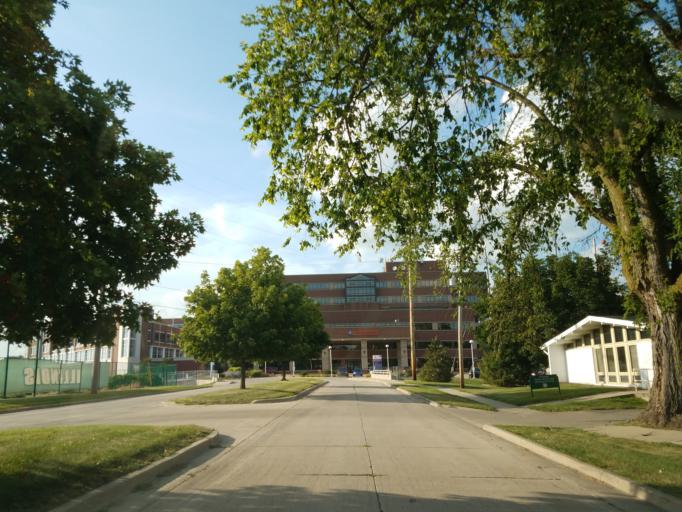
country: US
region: Illinois
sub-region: McLean County
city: Bloomington
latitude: 40.4956
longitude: -88.9908
